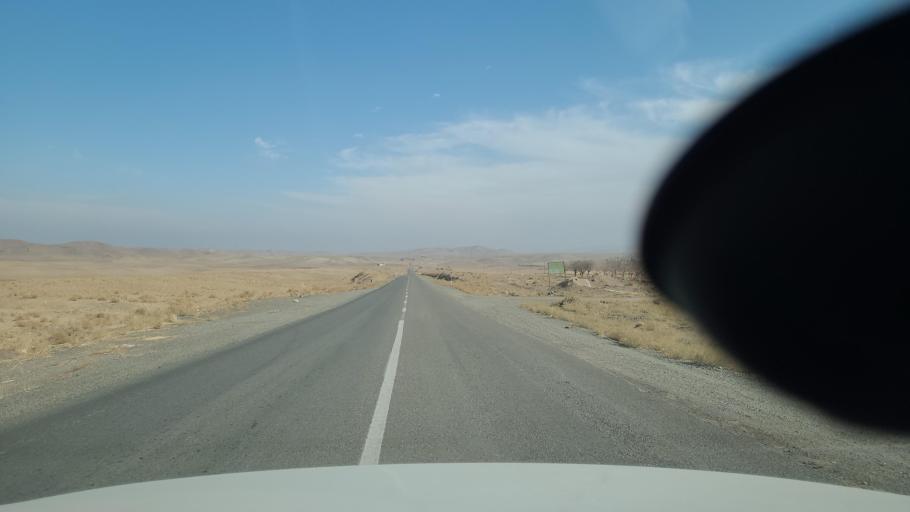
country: IR
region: Razavi Khorasan
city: Fariman
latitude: 35.5957
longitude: 59.7277
